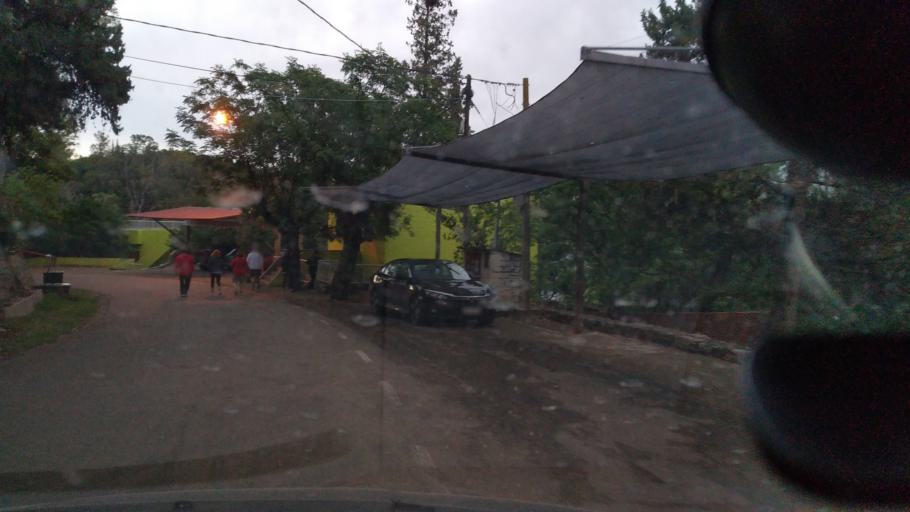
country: AR
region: Cordoba
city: Villa Las Rosas
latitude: -31.8714
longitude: -65.0326
